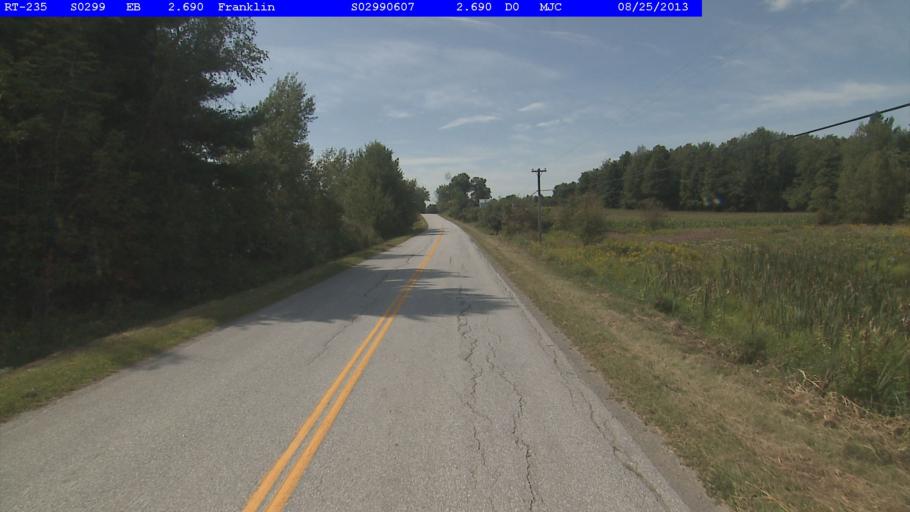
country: CA
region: Quebec
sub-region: Monteregie
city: Bedford
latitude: 45.0023
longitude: -72.9537
